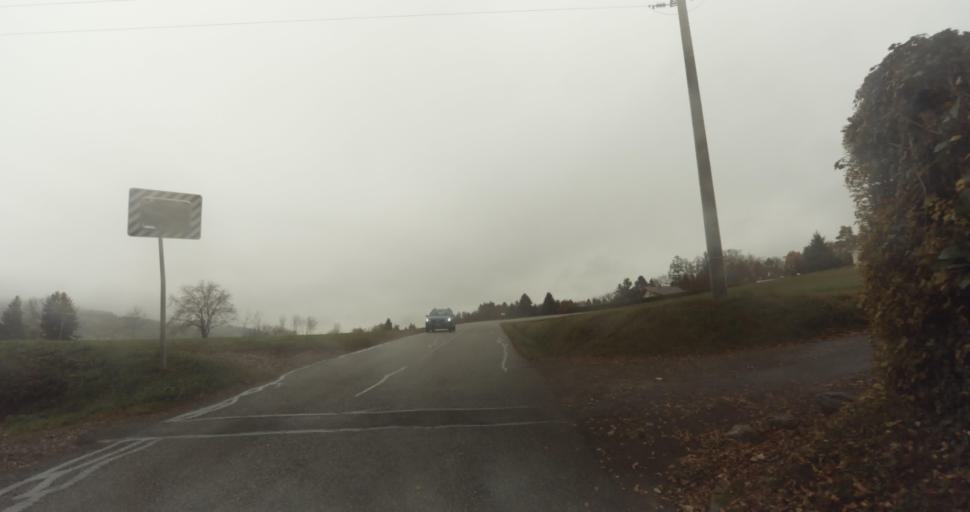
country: FR
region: Rhone-Alpes
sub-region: Departement de la Haute-Savoie
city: Villaz
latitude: 45.9437
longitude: 6.1689
